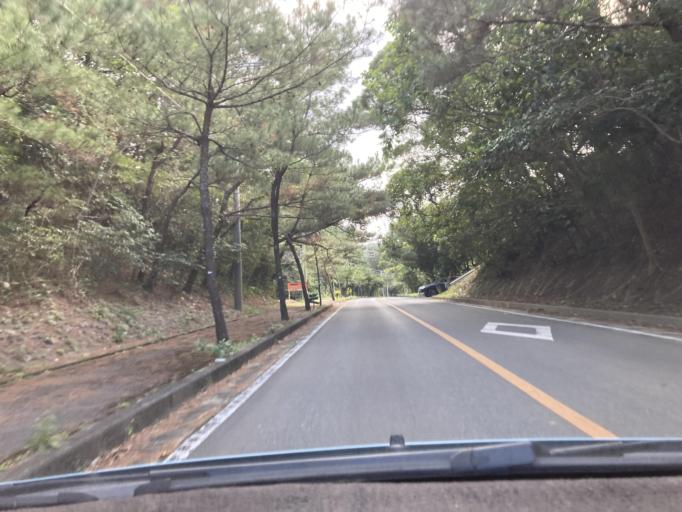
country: JP
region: Okinawa
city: Nago
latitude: 26.8560
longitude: 128.2602
